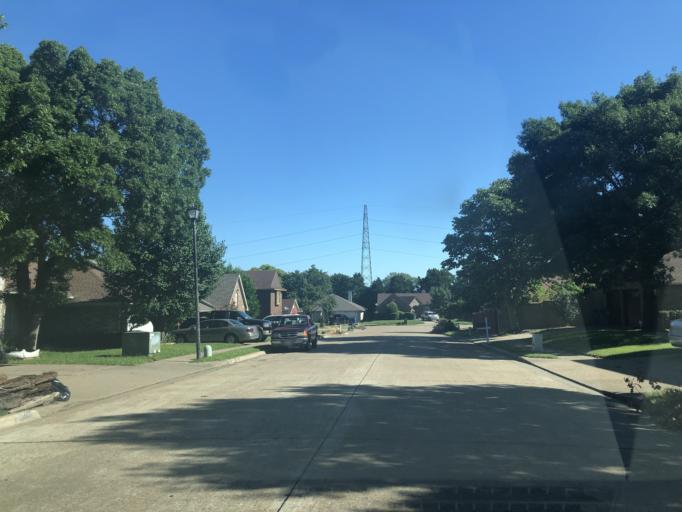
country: US
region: Texas
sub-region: Dallas County
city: Duncanville
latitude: 32.6674
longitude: -96.9343
